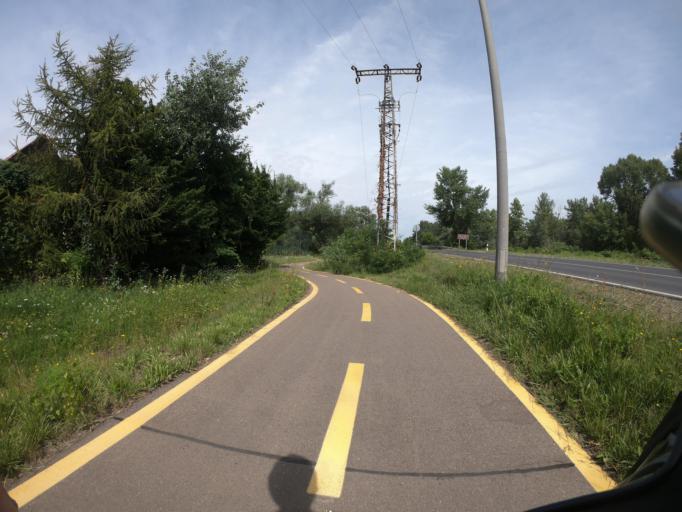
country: HU
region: Jasz-Nagykun-Szolnok
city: Tiszafured
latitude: 47.6292
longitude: 20.7468
